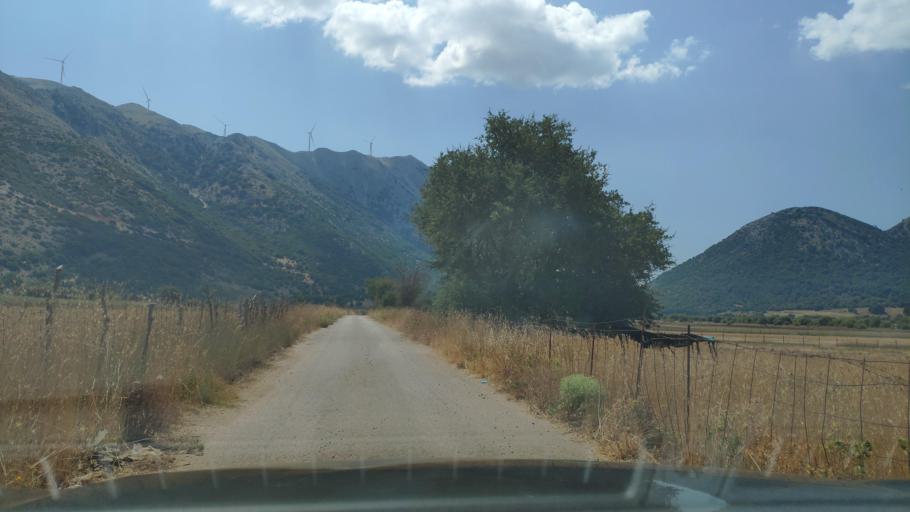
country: GR
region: West Greece
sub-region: Nomos Aitolias kai Akarnanias
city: Monastirakion
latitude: 38.7859
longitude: 20.9666
